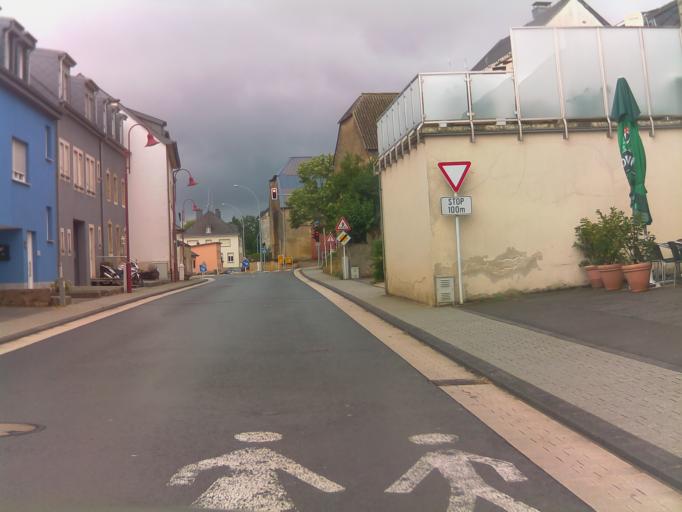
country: LU
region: Grevenmacher
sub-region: Canton de Remich
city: Dalheim
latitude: 49.5335
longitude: 6.2487
